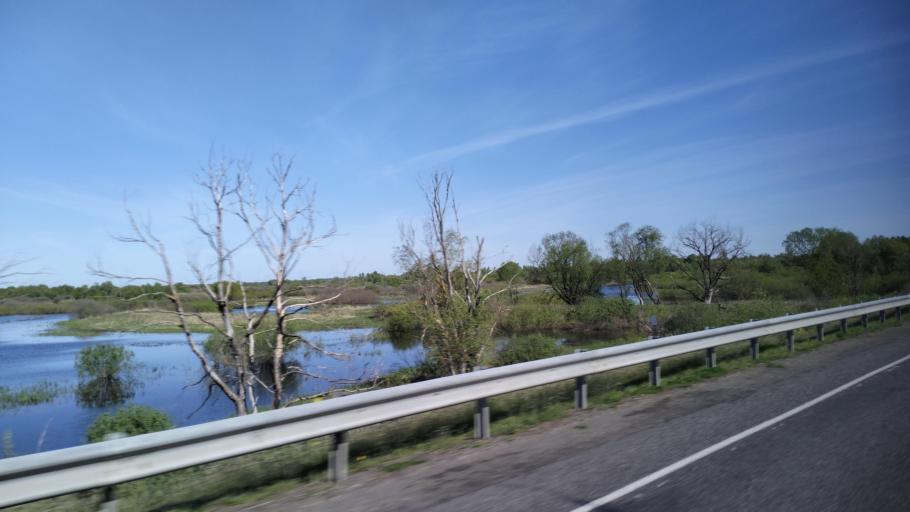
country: BY
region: Gomel
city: Turaw
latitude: 52.0871
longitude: 27.8279
